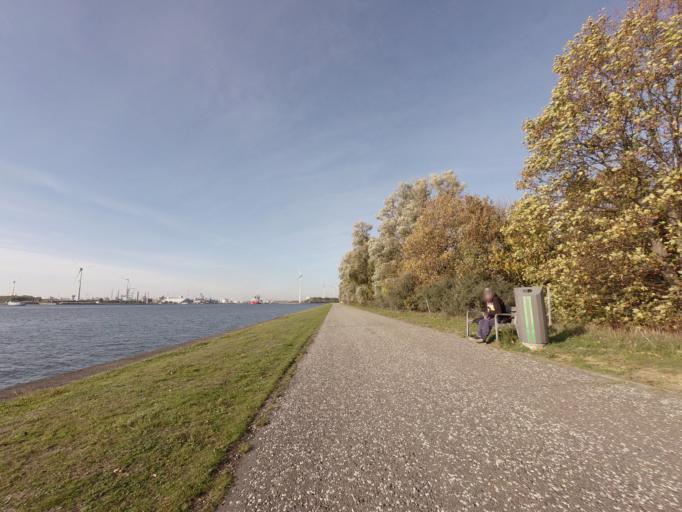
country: BE
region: Flanders
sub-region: Provincie Antwerpen
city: Stabroek
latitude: 51.3426
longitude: 4.3030
